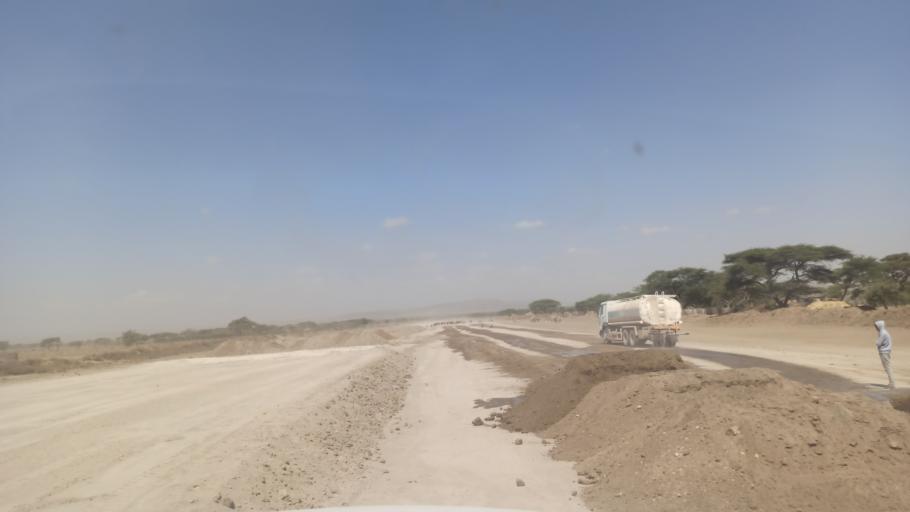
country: ET
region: Oromiya
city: Ziway
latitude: 7.7382
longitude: 38.6214
